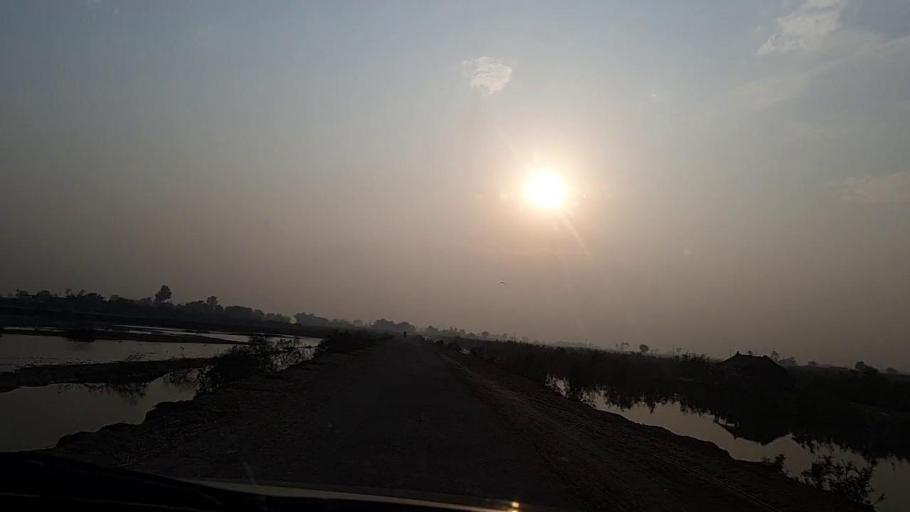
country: PK
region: Sindh
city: Nawabshah
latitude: 26.2980
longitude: 68.2591
